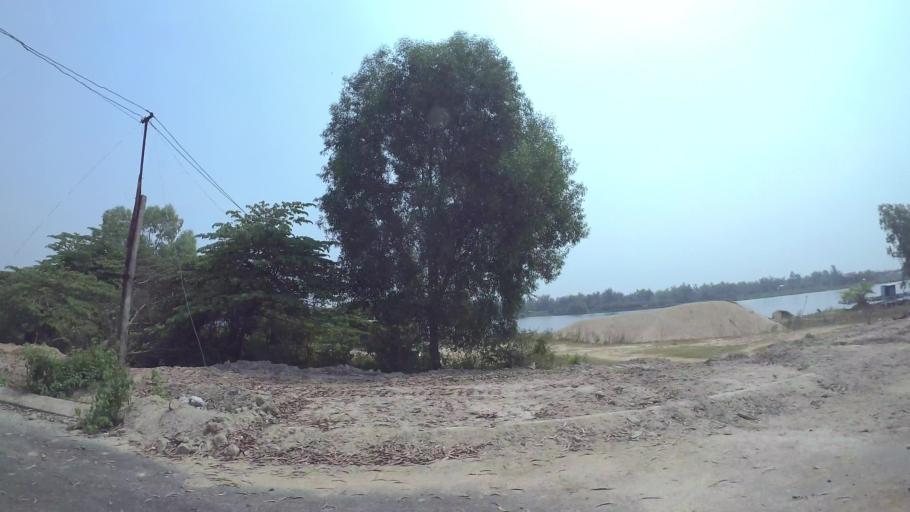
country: VN
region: Da Nang
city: Cam Le
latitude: 15.9792
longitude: 108.2204
